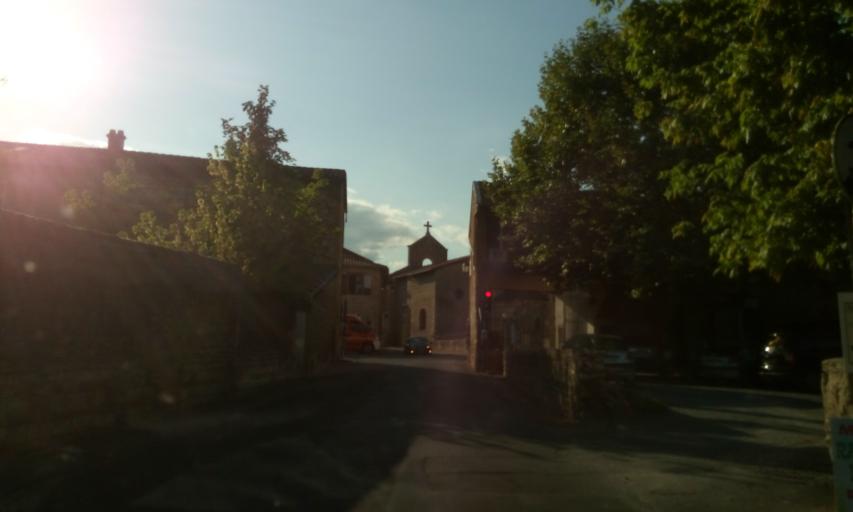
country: FR
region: Rhone-Alpes
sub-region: Departement du Rhone
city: Morance
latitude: 45.8977
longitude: 4.7011
